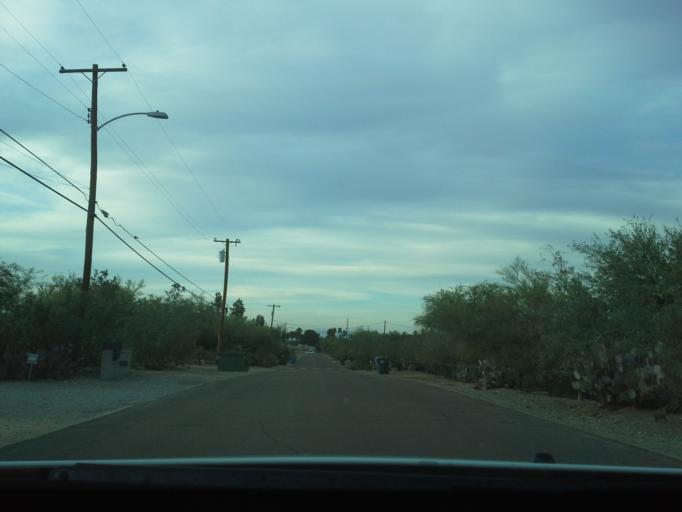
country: US
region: Arizona
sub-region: Maricopa County
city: Paradise Valley
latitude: 33.5796
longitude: -112.0022
